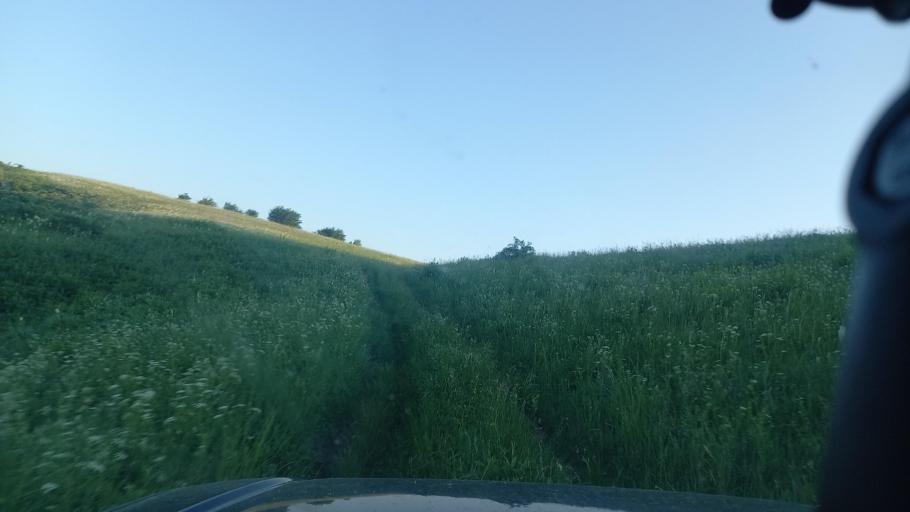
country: RU
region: Karachayevo-Cherkesiya
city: Kurdzhinovo
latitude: 44.1268
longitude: 41.0883
